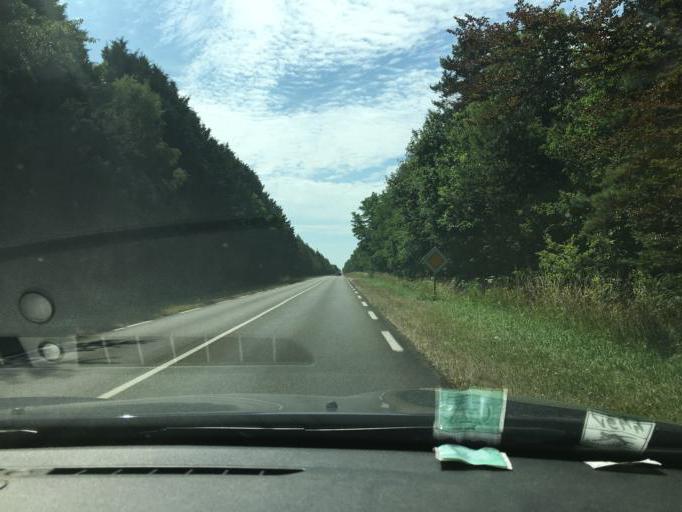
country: FR
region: Centre
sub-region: Departement du Loiret
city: La Ferte-Saint-Aubin
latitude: 47.6705
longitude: 1.9727
